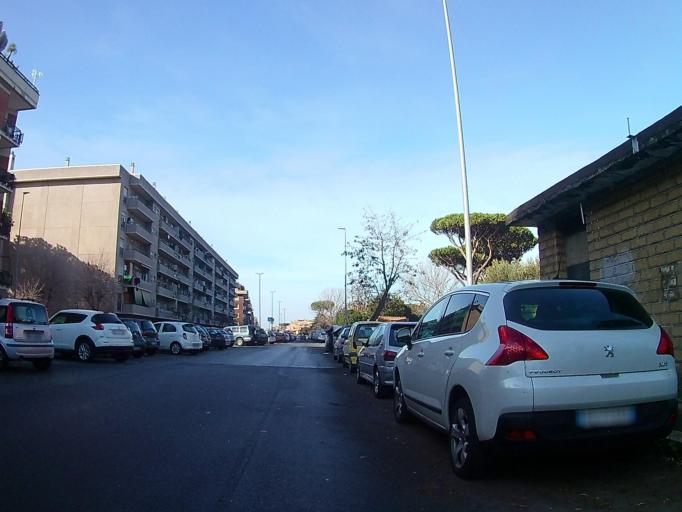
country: IT
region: Latium
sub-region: Citta metropolitana di Roma Capitale
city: Lido di Ostia
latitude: 41.7351
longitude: 12.2989
